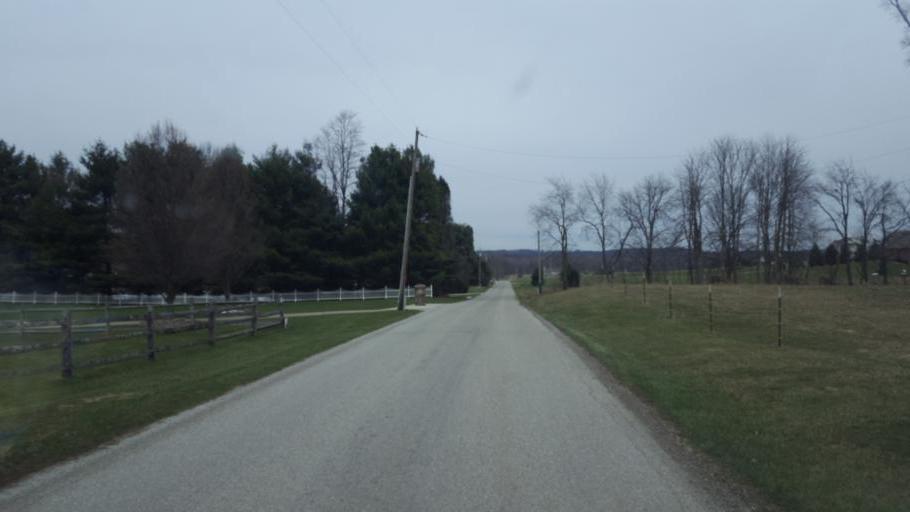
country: US
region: Ohio
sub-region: Sandusky County
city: Bellville
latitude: 40.6042
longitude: -82.5680
